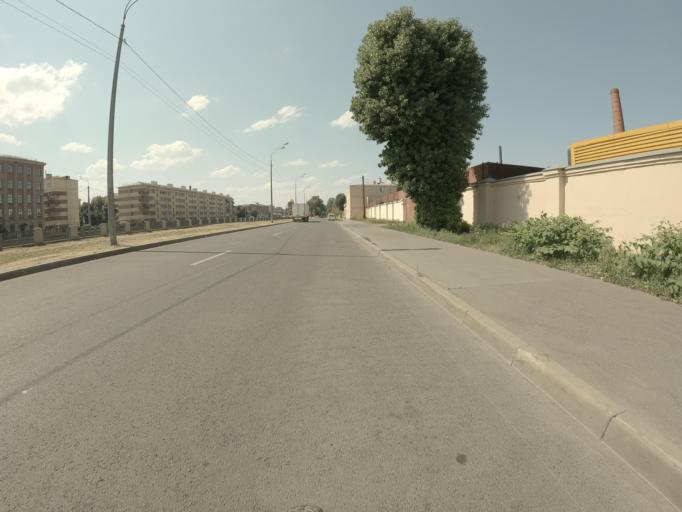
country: RU
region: St.-Petersburg
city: Admiralteisky
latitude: 59.9095
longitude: 30.2688
